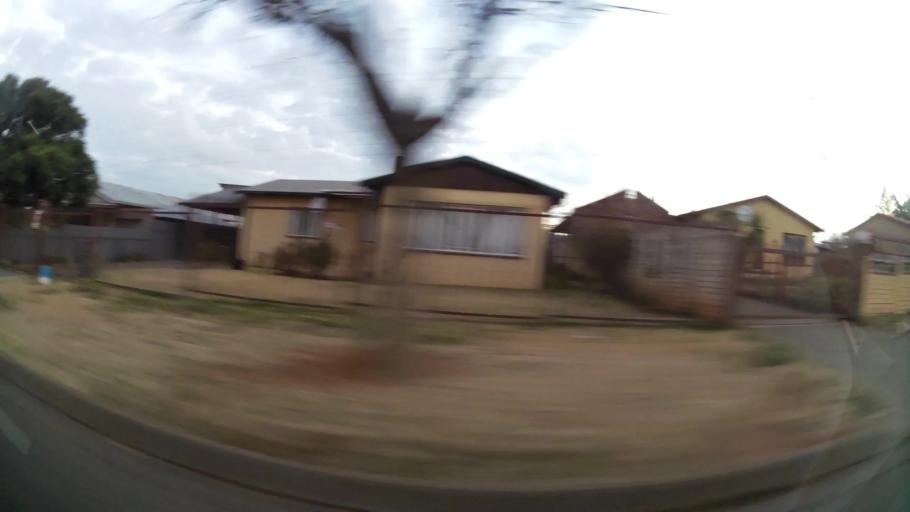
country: ZA
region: Orange Free State
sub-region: Mangaung Metropolitan Municipality
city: Bloemfontein
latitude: -29.1639
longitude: 26.1990
